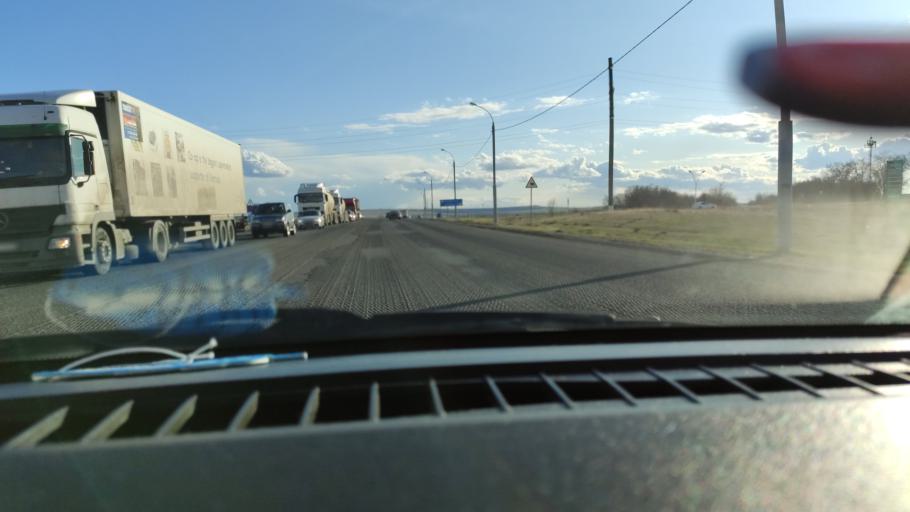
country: RU
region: Saratov
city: Yelshanka
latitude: 51.8136
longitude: 46.2069
